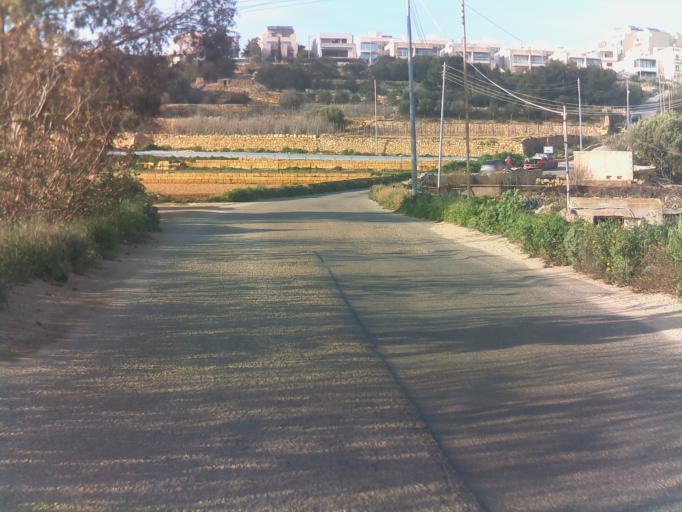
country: MT
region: L-Imgarr
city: Imgarr
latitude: 35.9367
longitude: 14.3510
